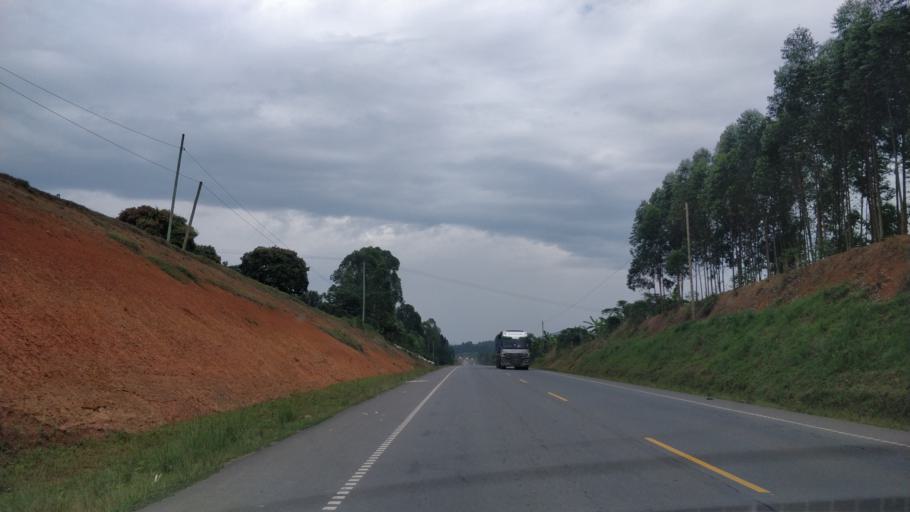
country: UG
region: Western Region
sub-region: Sheema District
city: Kibingo
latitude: -0.6704
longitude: 30.4360
